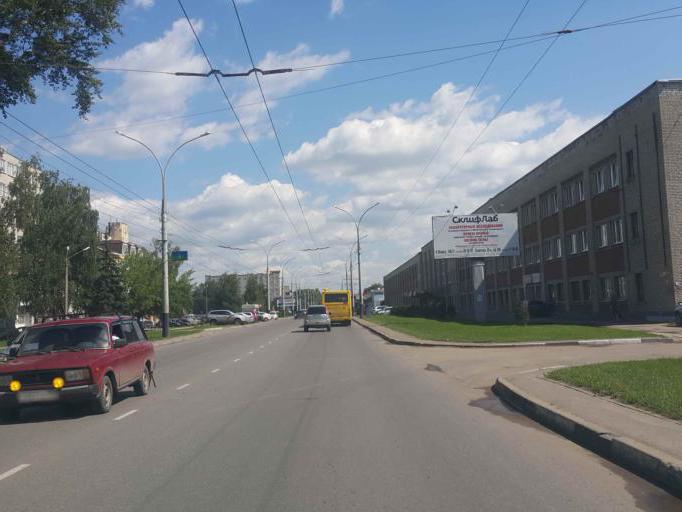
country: RU
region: Tambov
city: Tambov
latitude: 52.7461
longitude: 41.4559
